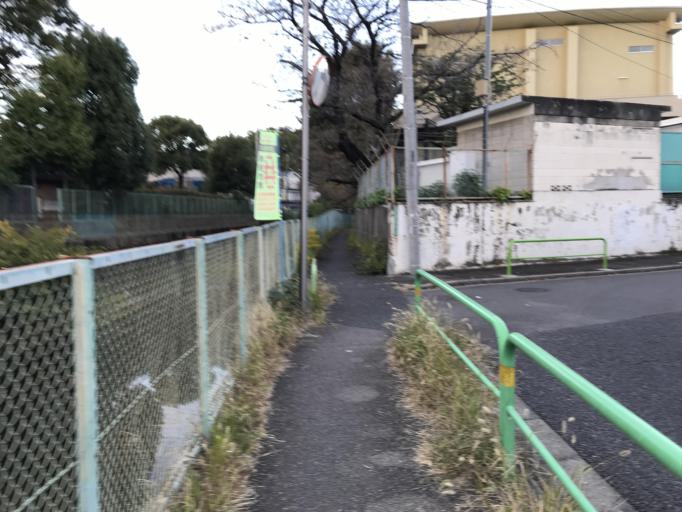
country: JP
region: Saitama
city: Wako
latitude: 35.7678
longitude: 139.6111
